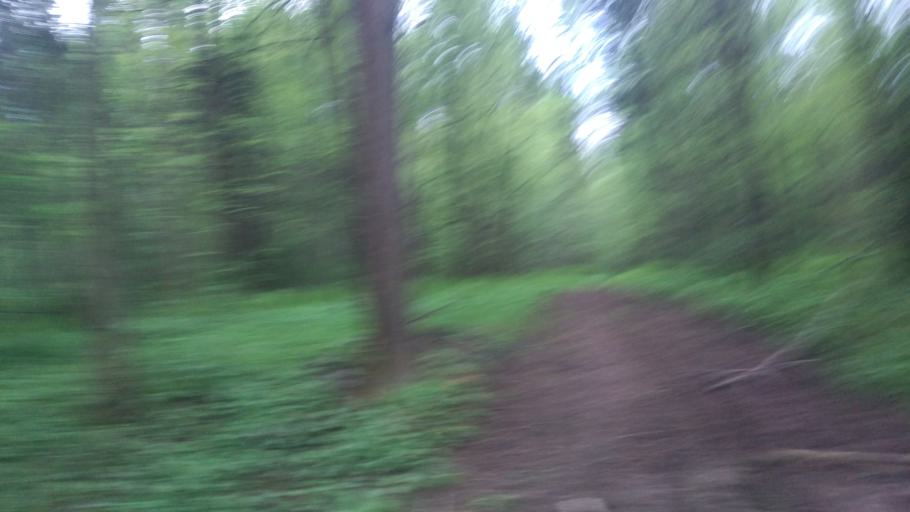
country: RU
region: Perm
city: Froly
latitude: 57.9634
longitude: 56.2992
